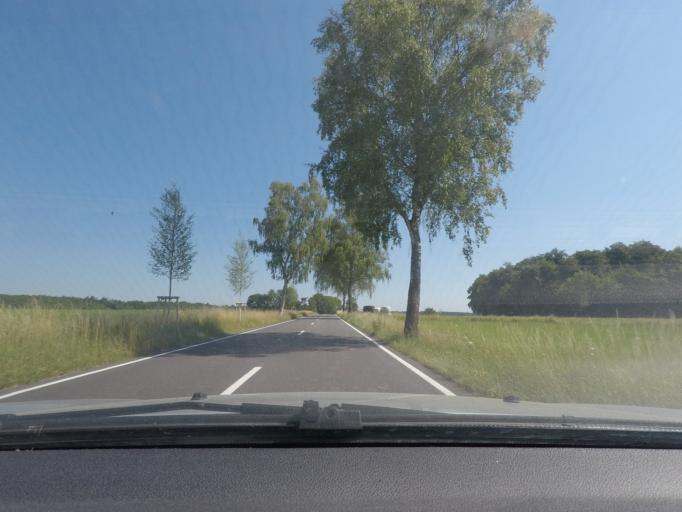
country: LU
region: Diekirch
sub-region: Canton de Redange
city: Ell
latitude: 49.7361
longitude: 5.8454
